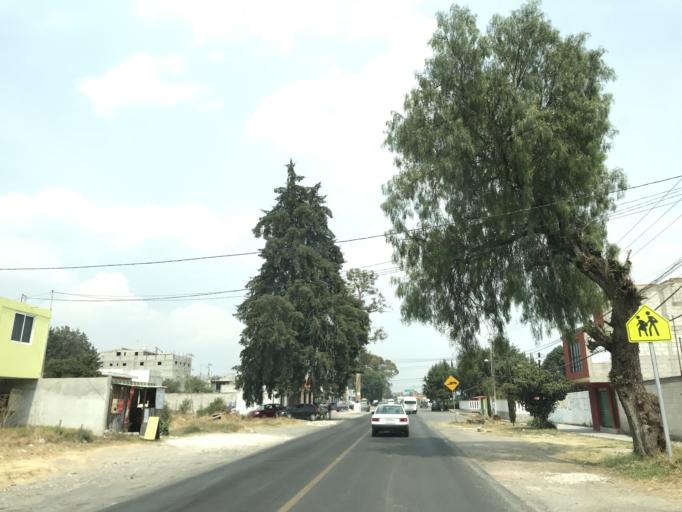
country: MX
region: Tlaxcala
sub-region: Panotla
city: Fraccionamiento la Virgen
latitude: 19.3194
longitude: -98.2752
